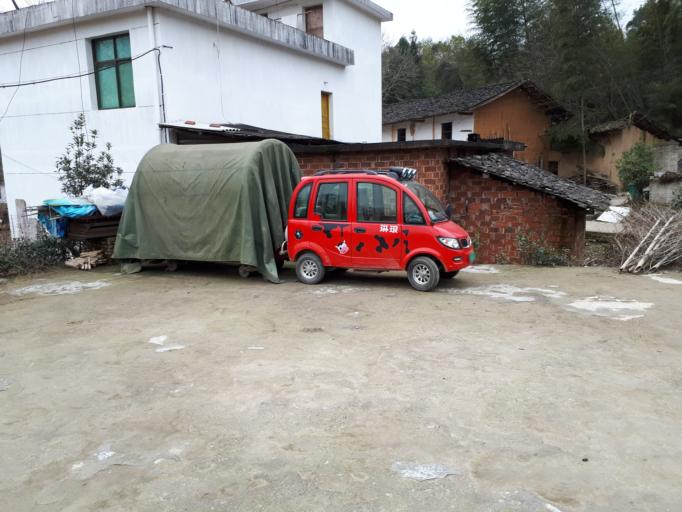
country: CN
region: Jiangxi Sheng
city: Wenquan
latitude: 28.5303
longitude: 114.3107
